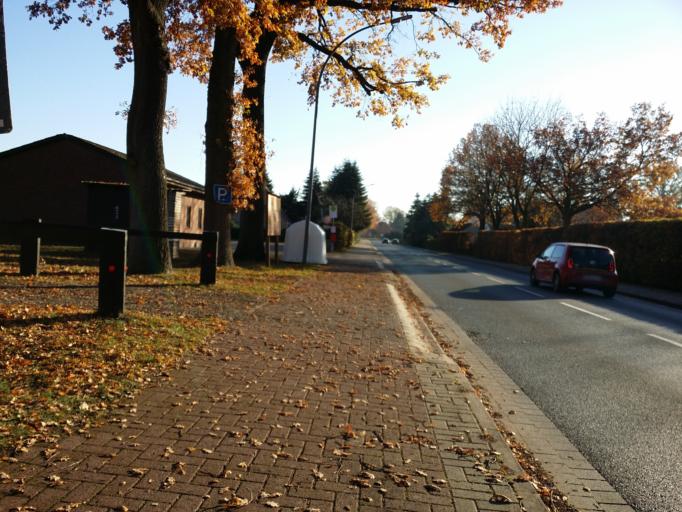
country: DE
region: Lower Saxony
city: Langwedel
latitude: 53.0339
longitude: 9.1567
